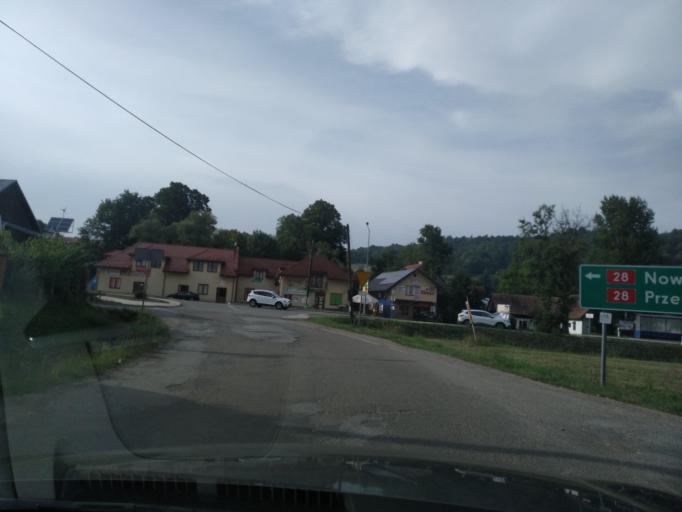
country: PL
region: Subcarpathian Voivodeship
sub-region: Powiat sanocki
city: Tyrawa Woloska
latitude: 49.5766
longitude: 22.3682
